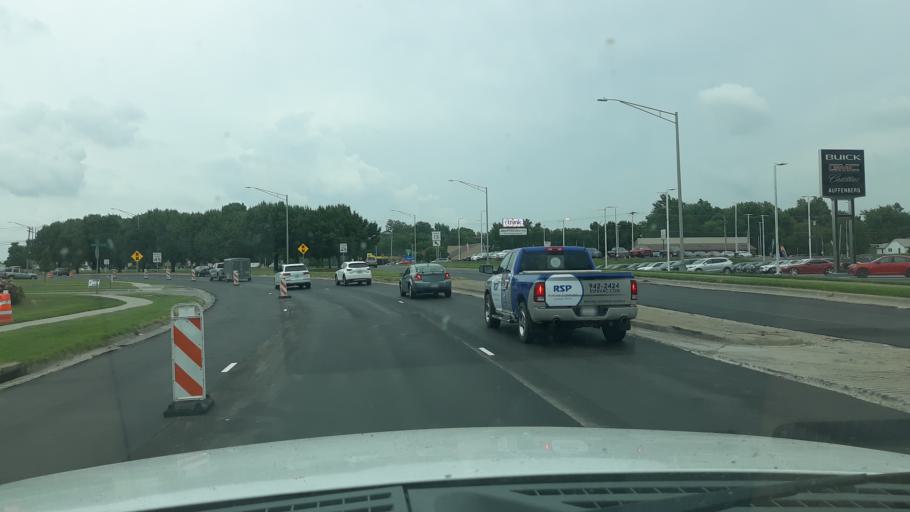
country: US
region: Illinois
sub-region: Jackson County
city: Carbondale
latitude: 37.7267
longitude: -89.2015
